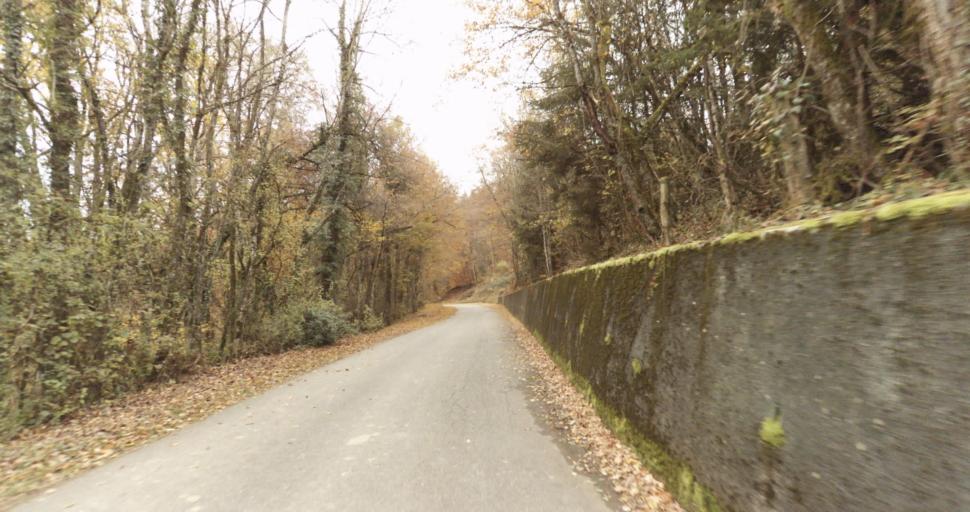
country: FR
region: Rhone-Alpes
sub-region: Departement de la Haute-Savoie
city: Chavanod
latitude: 45.8721
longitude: 6.0374
